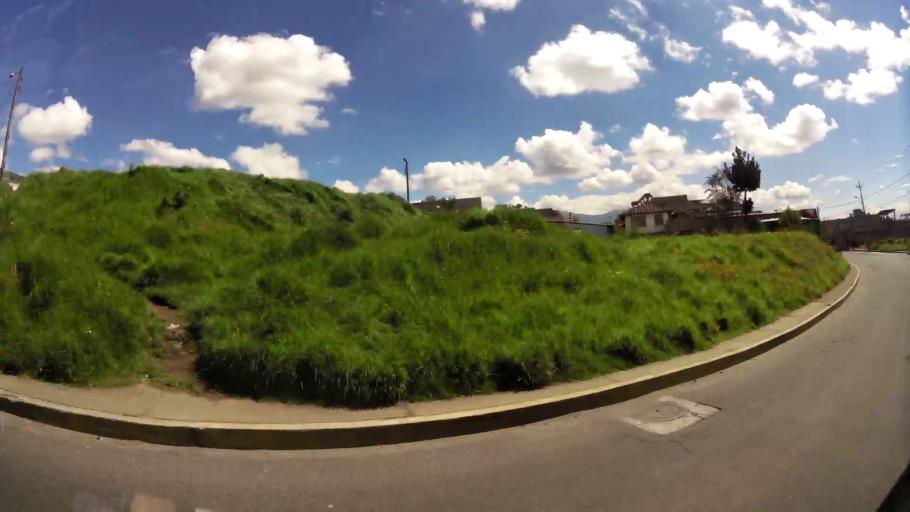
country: EC
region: Pichincha
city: Quito
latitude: -0.3160
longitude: -78.5626
